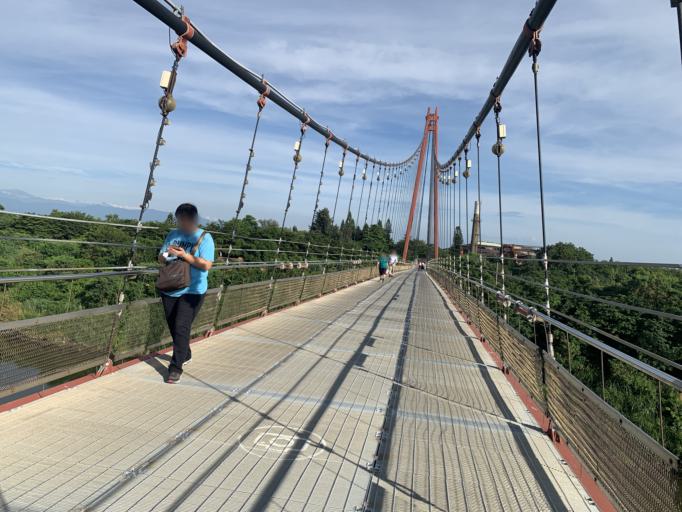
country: TW
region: Taiwan
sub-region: Chiayi
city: Taibao
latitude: 23.4829
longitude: 120.2954
